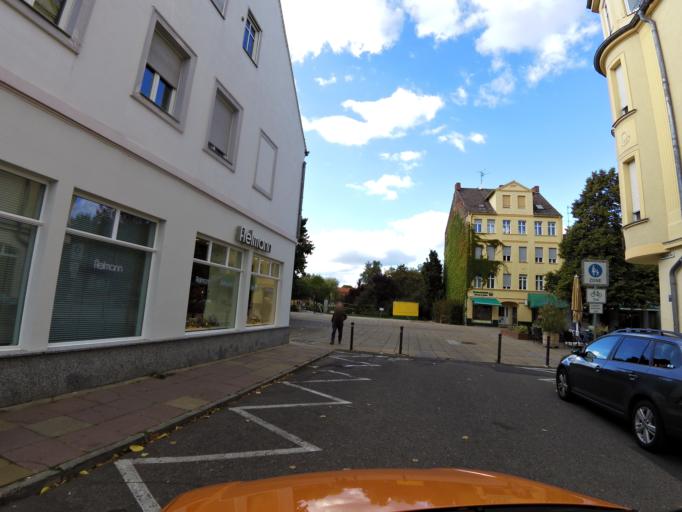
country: DE
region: Brandenburg
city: Luckenwalde
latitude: 52.0879
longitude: 13.1725
